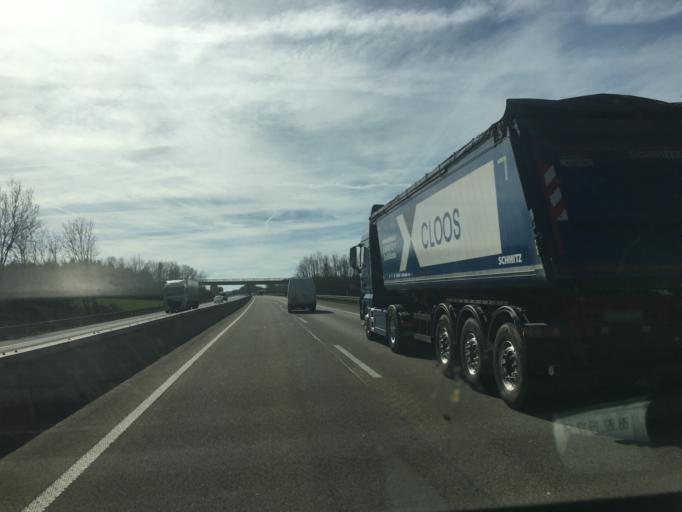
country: DE
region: North Rhine-Westphalia
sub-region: Regierungsbezirk Koln
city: Mechernich
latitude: 50.5637
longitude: 6.6815
